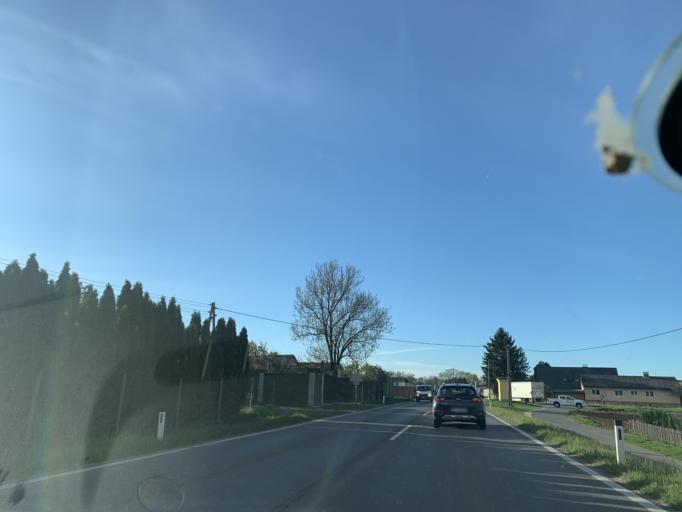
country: AT
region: Styria
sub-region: Politischer Bezirk Leibnitz
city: Kaindorf an der Sulm
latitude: 46.8100
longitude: 15.5283
